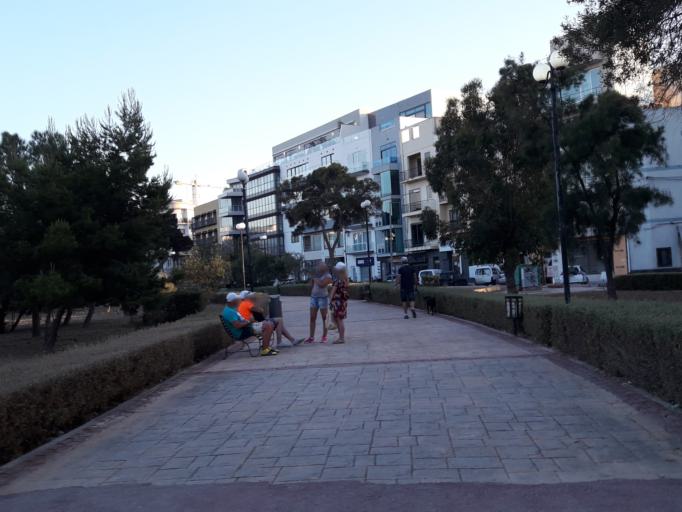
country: MT
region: Ta' Xbiex
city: Ta' Xbiex
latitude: 35.9028
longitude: 14.4950
